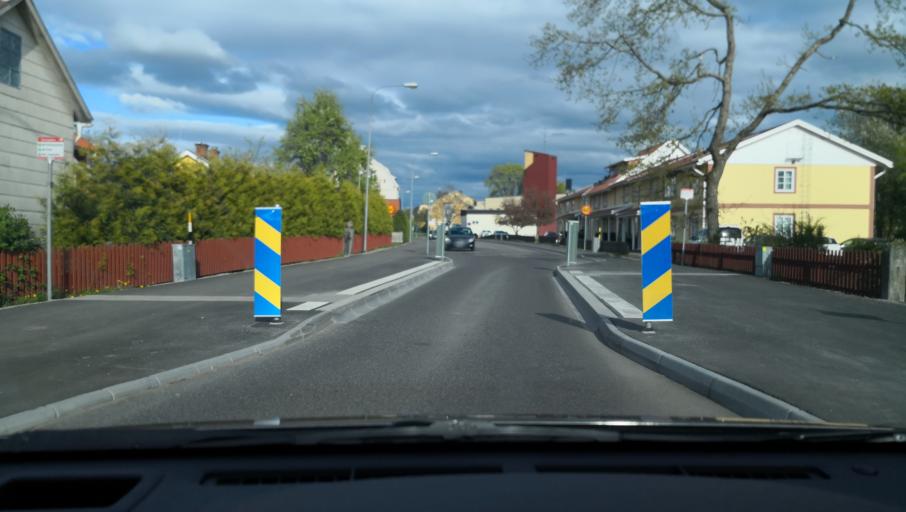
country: SE
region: Dalarna
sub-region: Hedemora Kommun
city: Hedemora
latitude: 60.2783
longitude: 15.9784
